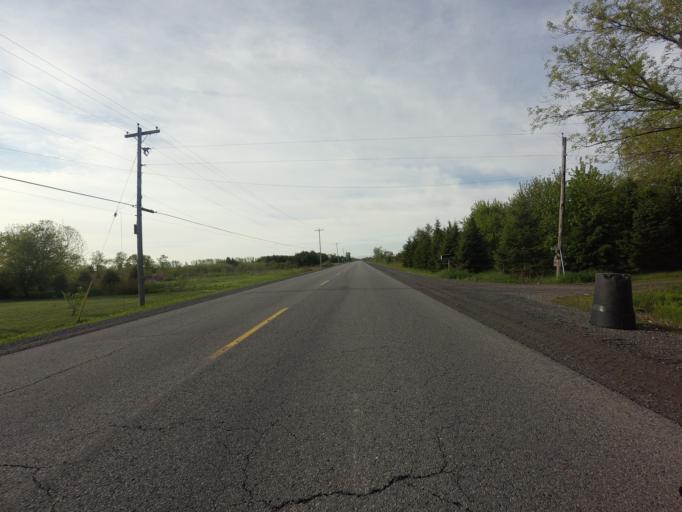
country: CA
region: Ontario
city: Ottawa
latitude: 45.3075
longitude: -75.4577
